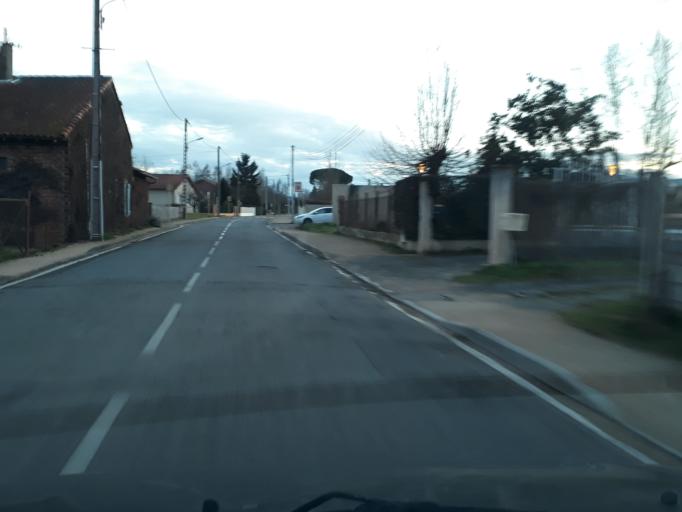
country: FR
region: Midi-Pyrenees
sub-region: Departement de la Haute-Garonne
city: Carbonne
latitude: 43.3023
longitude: 1.2288
